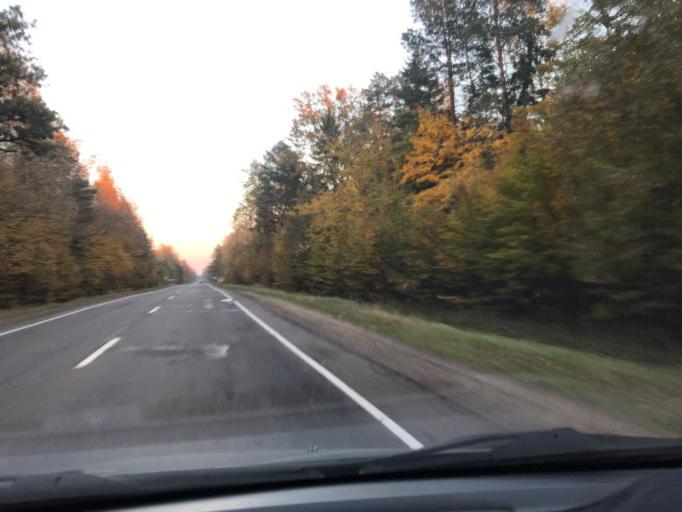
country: BY
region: Mogilev
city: Hlusha
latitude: 53.0895
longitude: 28.8869
